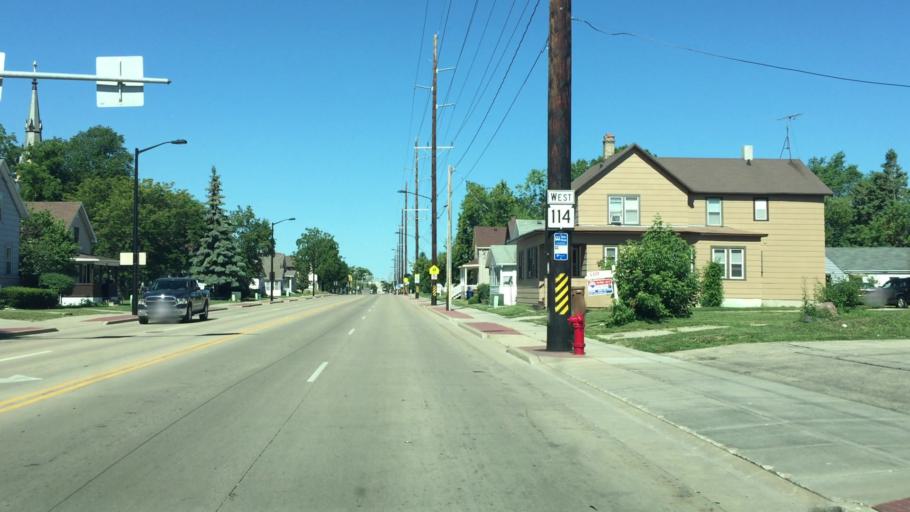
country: US
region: Wisconsin
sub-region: Winnebago County
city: Menasha
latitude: 44.2047
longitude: -88.4405
